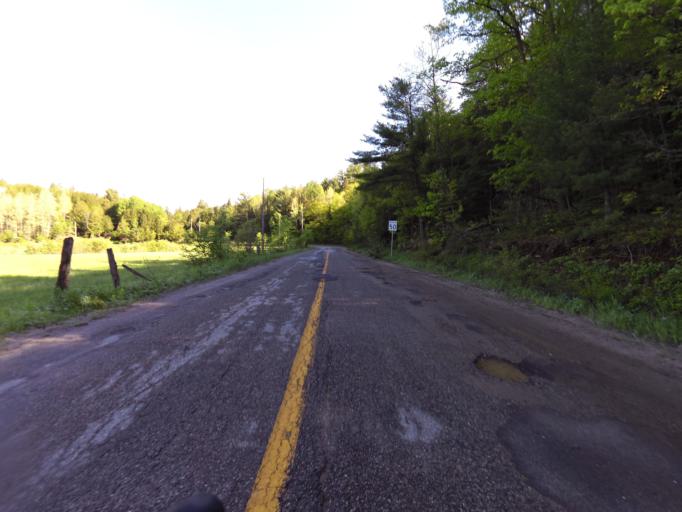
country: CA
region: Quebec
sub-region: Outaouais
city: Wakefield
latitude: 45.6189
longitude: -75.8798
